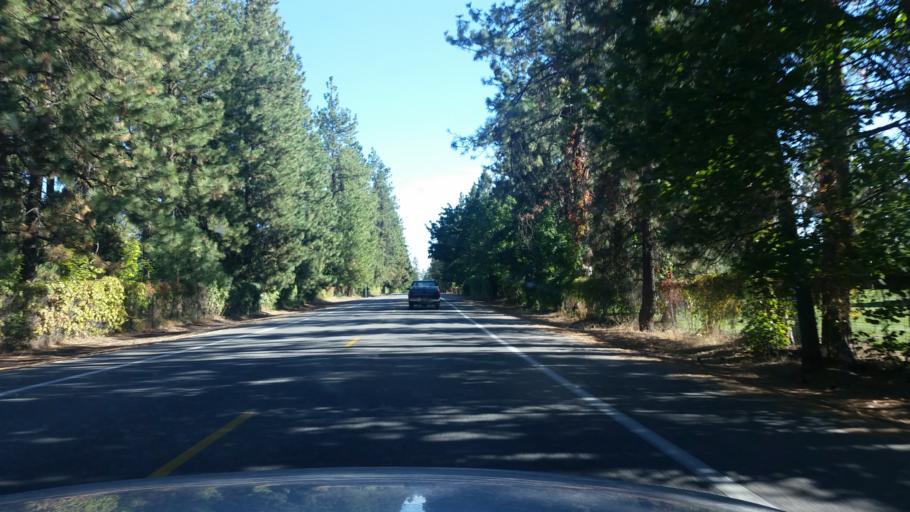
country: US
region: Washington
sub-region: Spokane County
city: Spokane
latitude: 47.6109
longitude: -117.3979
